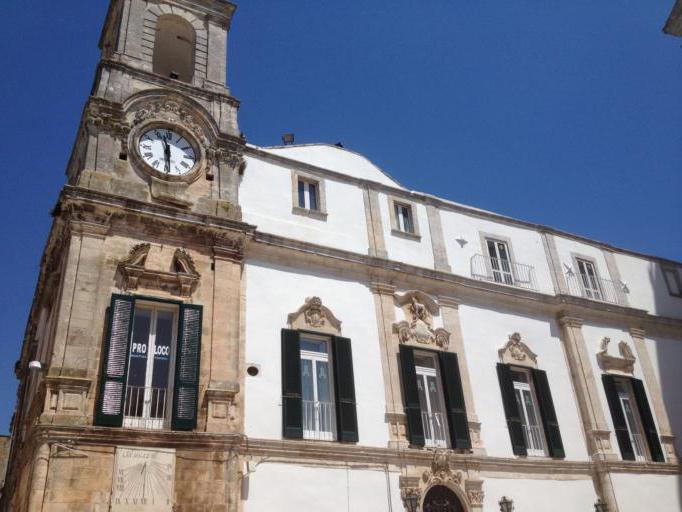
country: IT
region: Apulia
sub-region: Provincia di Taranto
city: Martina Franca
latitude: 40.7056
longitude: 17.3365
